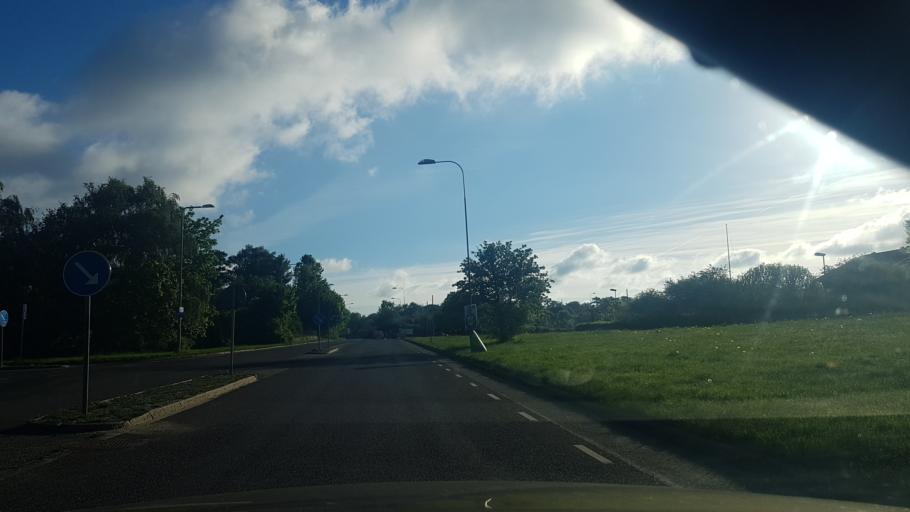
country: SE
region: Vaestra Goetaland
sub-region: Goteborg
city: Majorna
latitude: 57.6455
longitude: 11.8821
